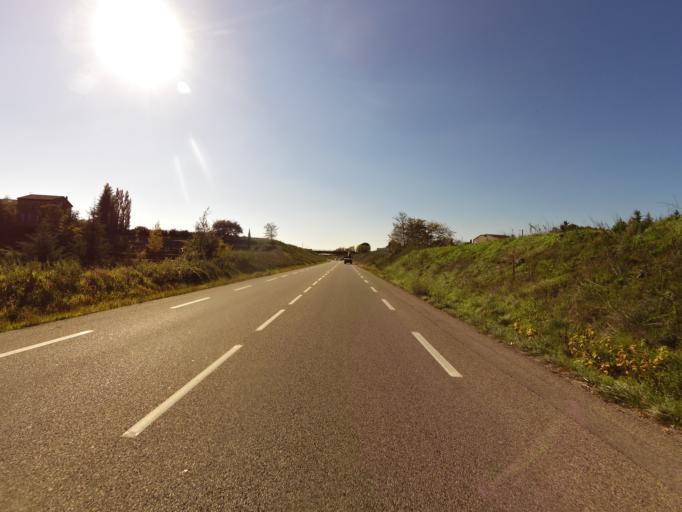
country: FR
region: Rhone-Alpes
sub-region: Departement de l'Ardeche
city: Saint-Privat
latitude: 44.6203
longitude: 4.4126
